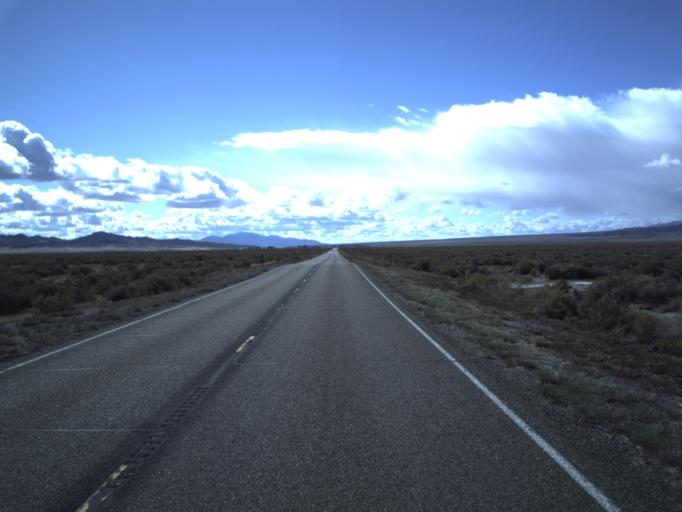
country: US
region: Nevada
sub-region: White Pine County
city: McGill
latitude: 39.0256
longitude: -114.0356
